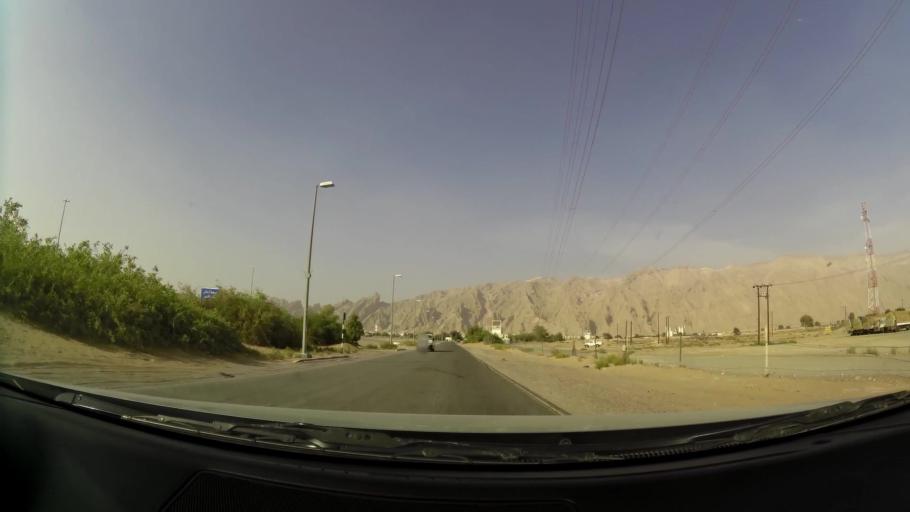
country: AE
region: Abu Dhabi
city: Al Ain
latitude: 24.0586
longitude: 55.7238
